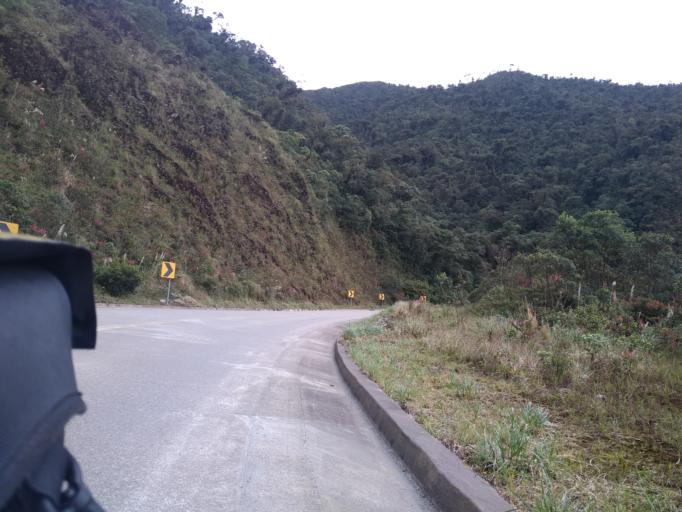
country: EC
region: Zamora-Chinchipe
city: Zamora
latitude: -4.4276
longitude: -79.1488
